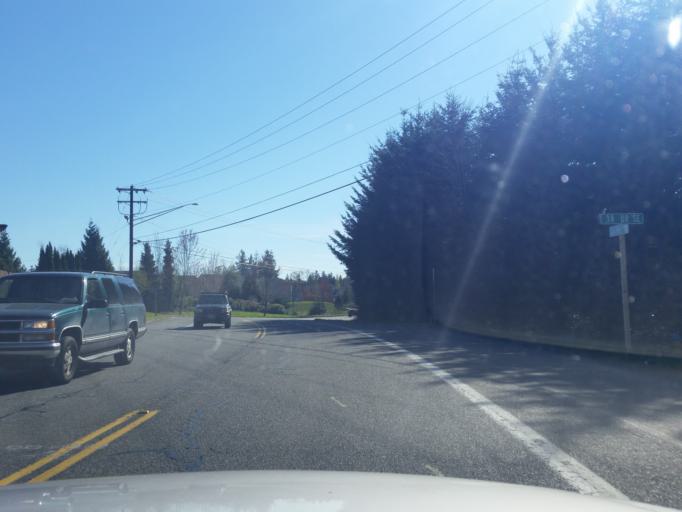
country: US
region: Washington
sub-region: Snohomish County
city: Mill Creek
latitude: 47.8627
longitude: -122.1806
